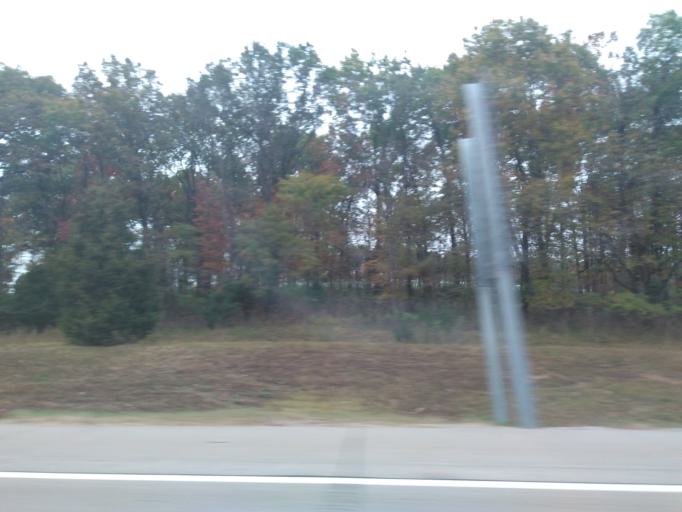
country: US
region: Missouri
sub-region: Saint Louis County
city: Oakville
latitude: 38.4909
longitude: -90.2902
